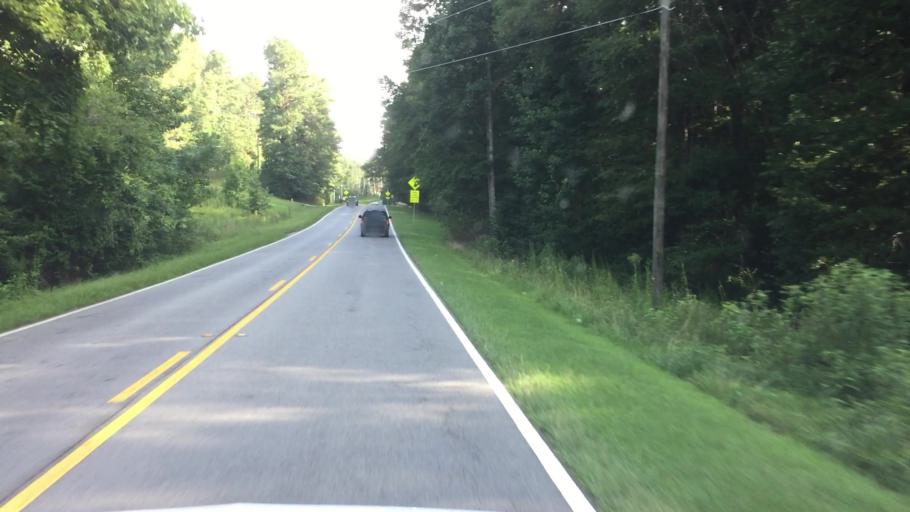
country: US
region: Georgia
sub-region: DeKalb County
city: Pine Mountain
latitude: 33.6268
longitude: -84.1300
